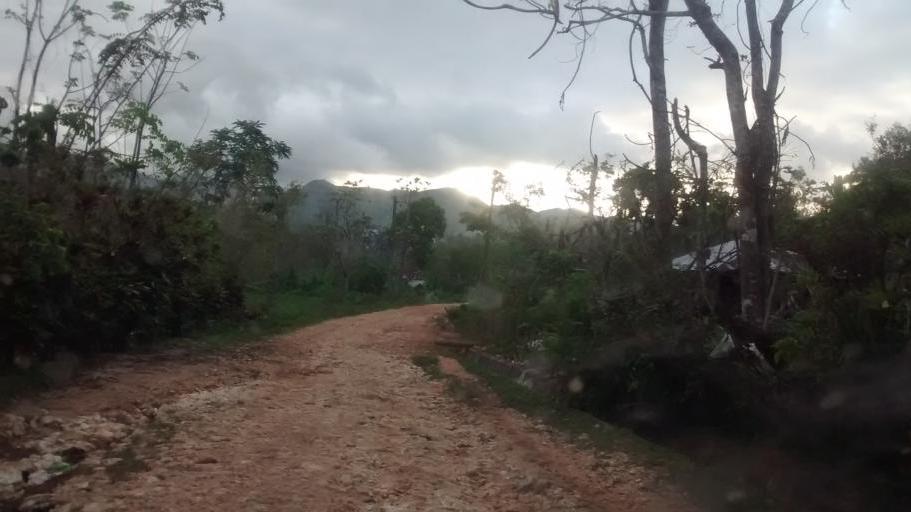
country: HT
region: Grandans
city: Corail
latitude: 18.4763
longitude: -73.7947
